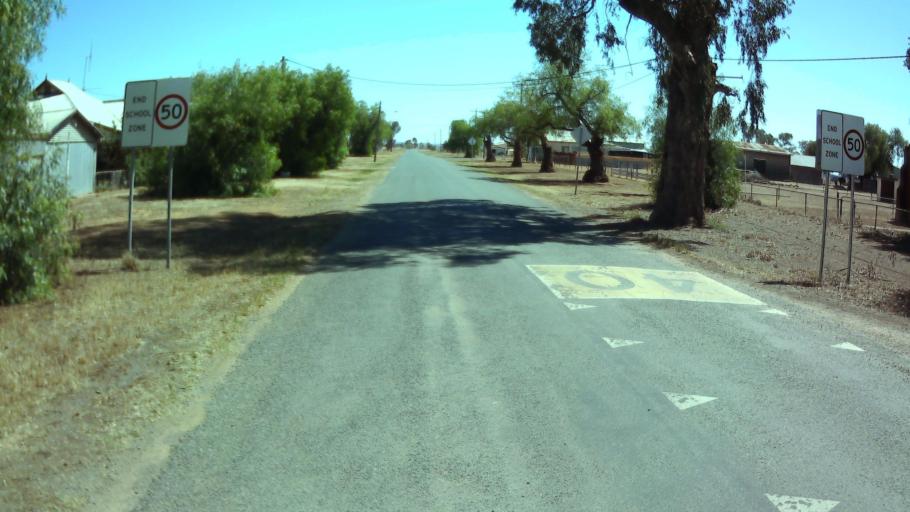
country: AU
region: New South Wales
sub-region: Weddin
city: Grenfell
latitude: -33.8442
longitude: 147.7438
